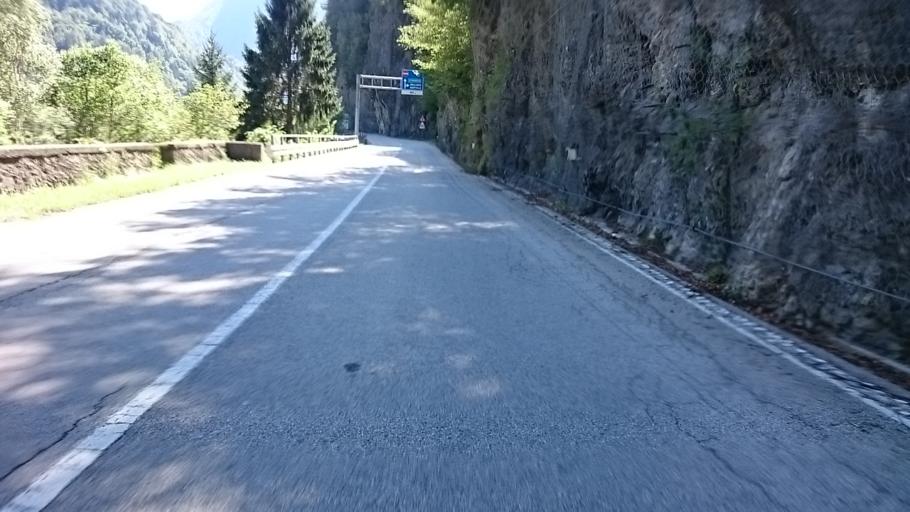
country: IT
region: Veneto
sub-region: Provincia di Belluno
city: Ospitale di Cadore
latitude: 46.3317
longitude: 12.3277
